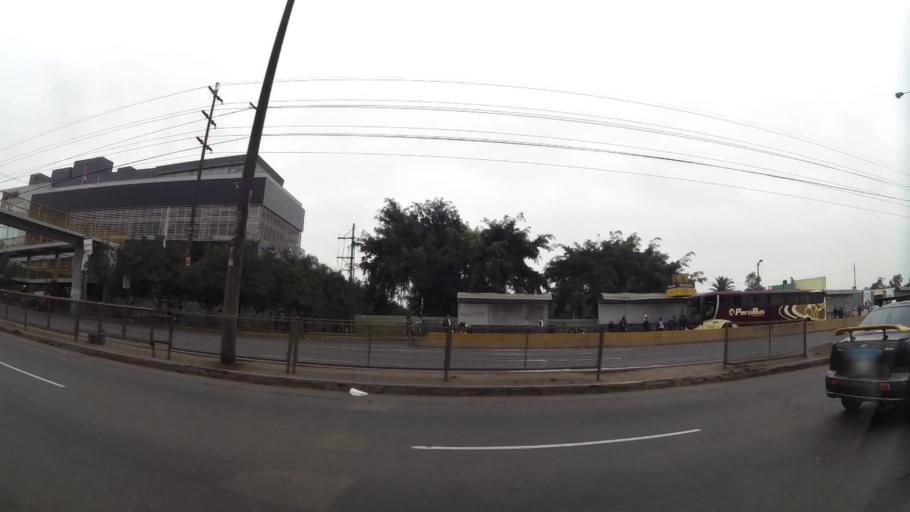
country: PE
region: Lima
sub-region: Lima
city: San Luis
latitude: -12.0813
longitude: -76.9861
